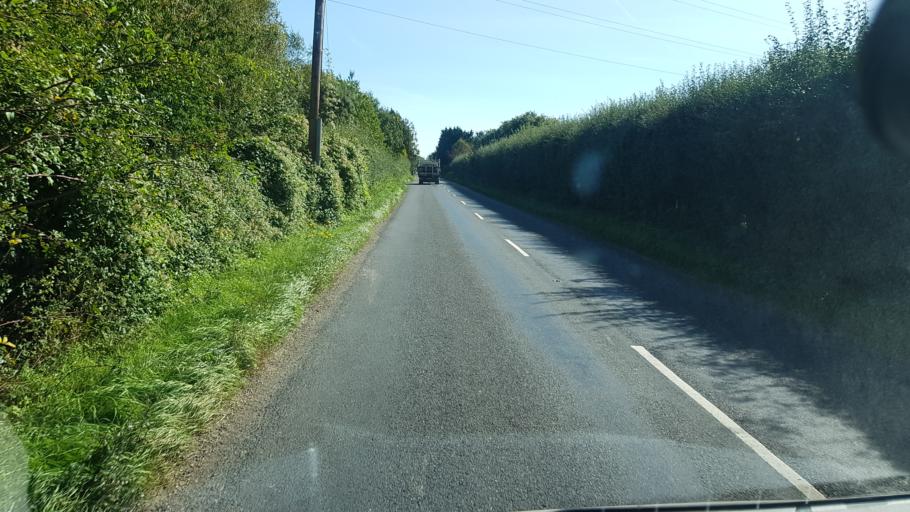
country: GB
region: England
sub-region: Kent
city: Yalding
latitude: 51.2381
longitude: 0.4721
